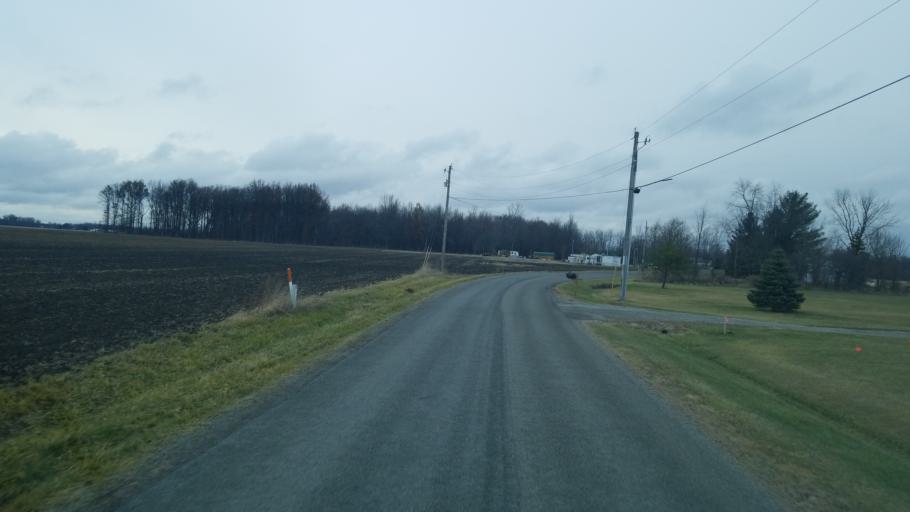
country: US
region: Ohio
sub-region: Union County
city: Richwood
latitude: 40.3262
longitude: -83.2505
